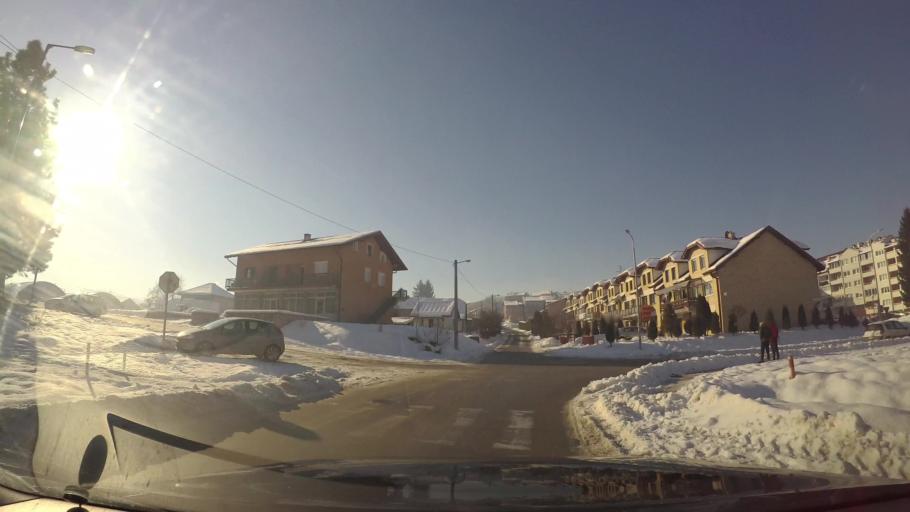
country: BA
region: Federation of Bosnia and Herzegovina
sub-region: Kanton Sarajevo
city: Sarajevo
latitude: 43.8233
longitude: 18.3733
